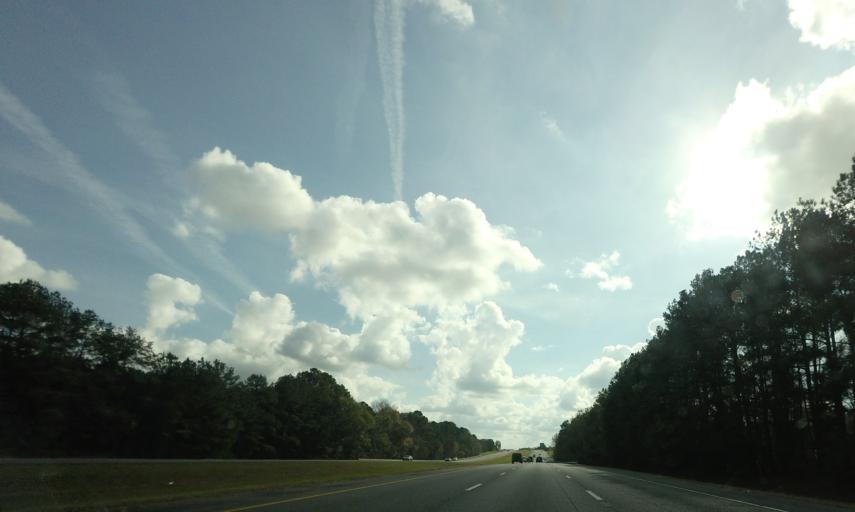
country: US
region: Georgia
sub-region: Dooly County
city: Unadilla
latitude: 32.3511
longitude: -83.7688
